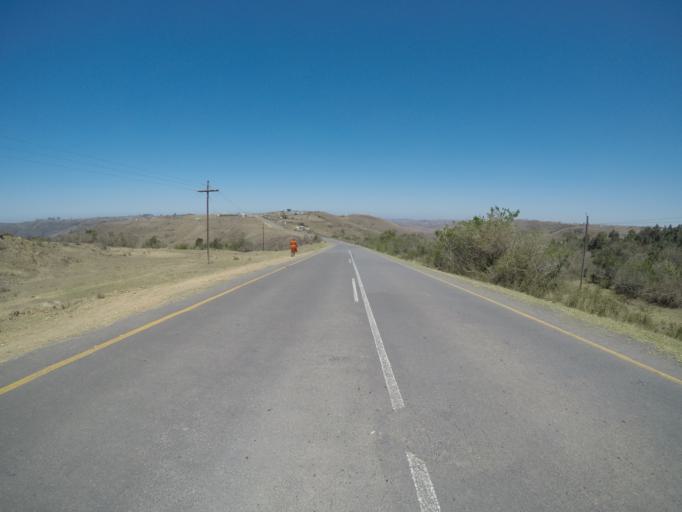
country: ZA
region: Eastern Cape
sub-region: OR Tambo District Municipality
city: Mthatha
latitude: -31.9003
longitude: 28.9459
